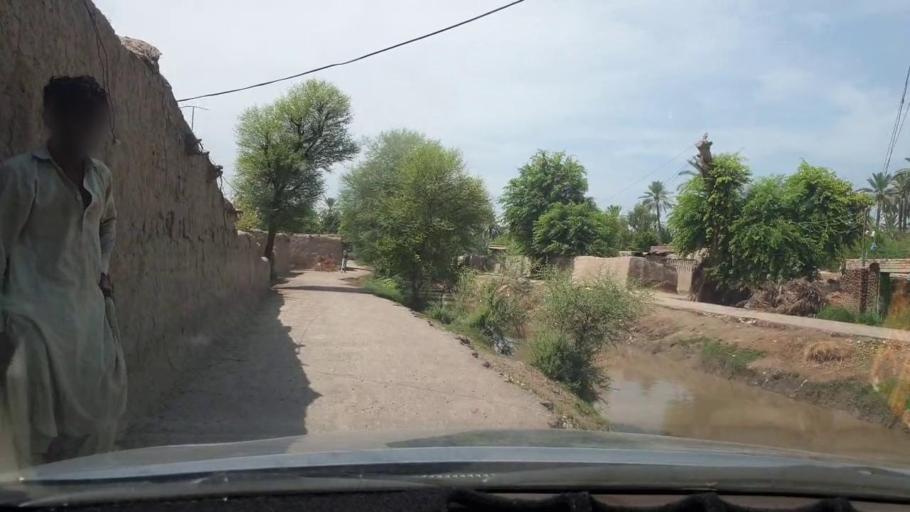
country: PK
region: Sindh
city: Khairpur
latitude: 27.4924
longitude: 68.7431
